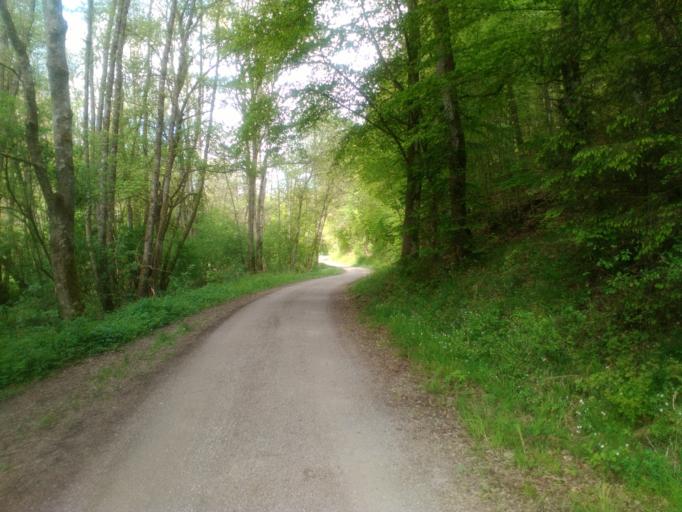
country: DE
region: Baden-Wuerttemberg
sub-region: Regierungsbezirk Stuttgart
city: Waldenbuch
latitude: 48.6051
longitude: 9.1620
